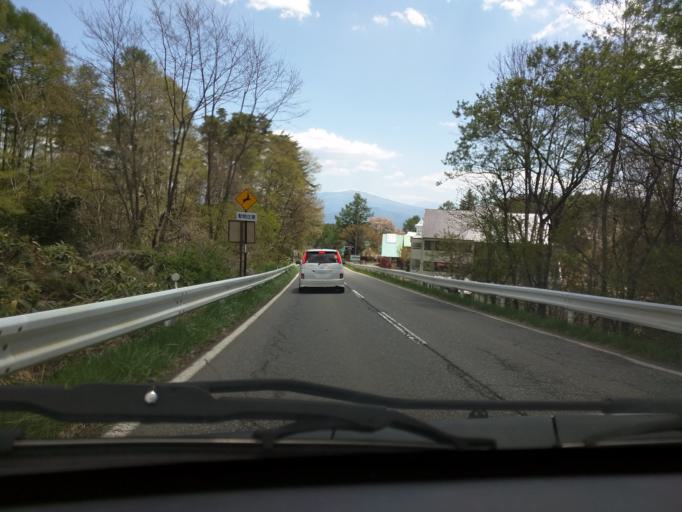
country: JP
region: Nagano
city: Nagano-shi
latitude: 36.7037
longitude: 138.1478
